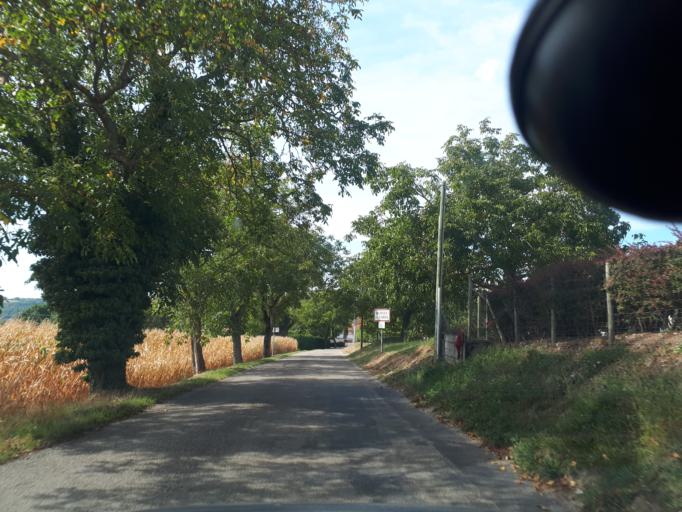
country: FR
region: Rhone-Alpes
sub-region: Departement de l'Isere
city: Chatonnay
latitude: 45.5104
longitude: 5.2057
